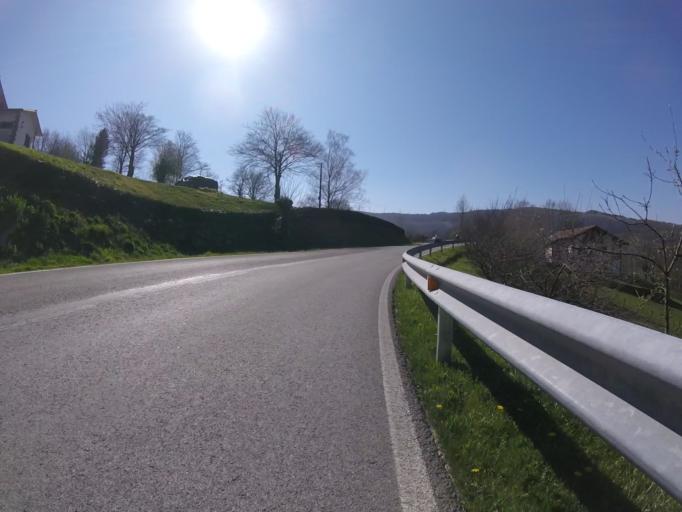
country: ES
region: Navarre
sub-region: Provincia de Navarra
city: Leitza
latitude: 43.0873
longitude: -1.8855
